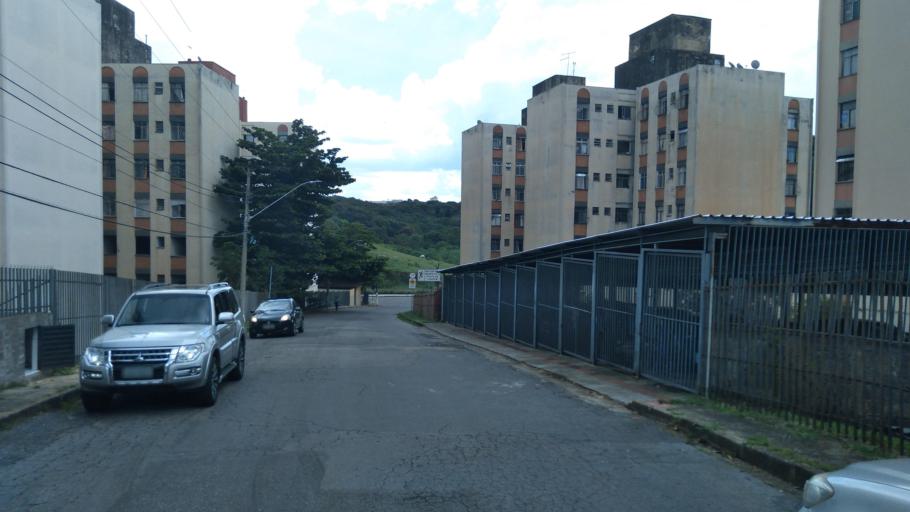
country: BR
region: Minas Gerais
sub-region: Contagem
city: Contagem
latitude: -19.9192
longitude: -44.0121
